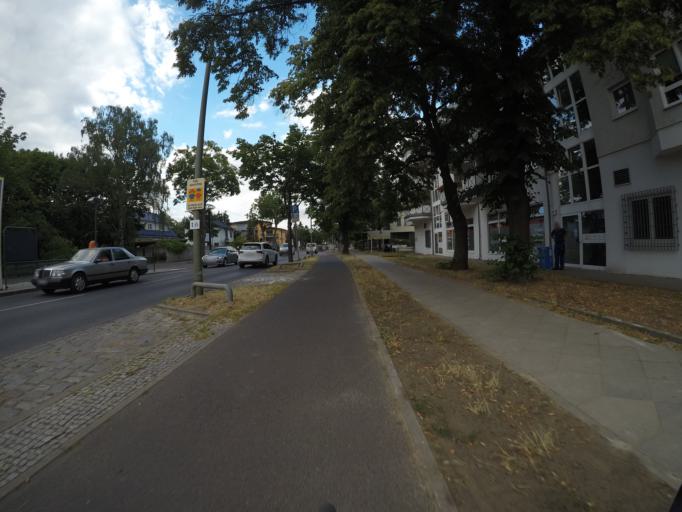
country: DE
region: Berlin
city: Mahlsdorf
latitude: 52.4829
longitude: 13.6019
